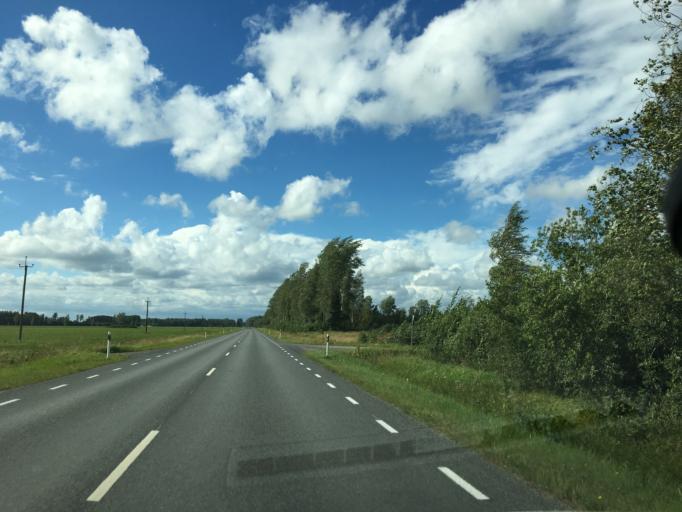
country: EE
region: Paernumaa
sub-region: Vaendra vald (alev)
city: Vandra
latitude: 58.5992
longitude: 25.1418
